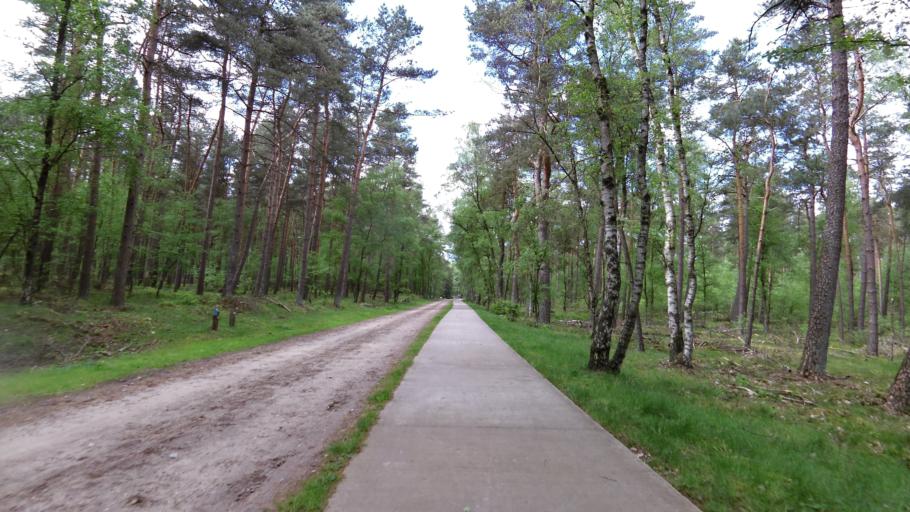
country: NL
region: Gelderland
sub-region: Gemeente Brummen
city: Eerbeek
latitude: 52.0747
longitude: 6.0574
